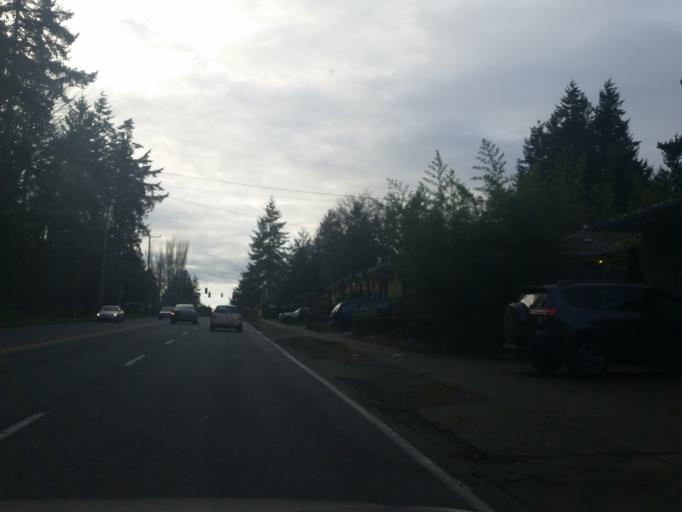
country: US
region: Washington
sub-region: King County
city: Shoreline
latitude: 47.7232
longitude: -122.3266
